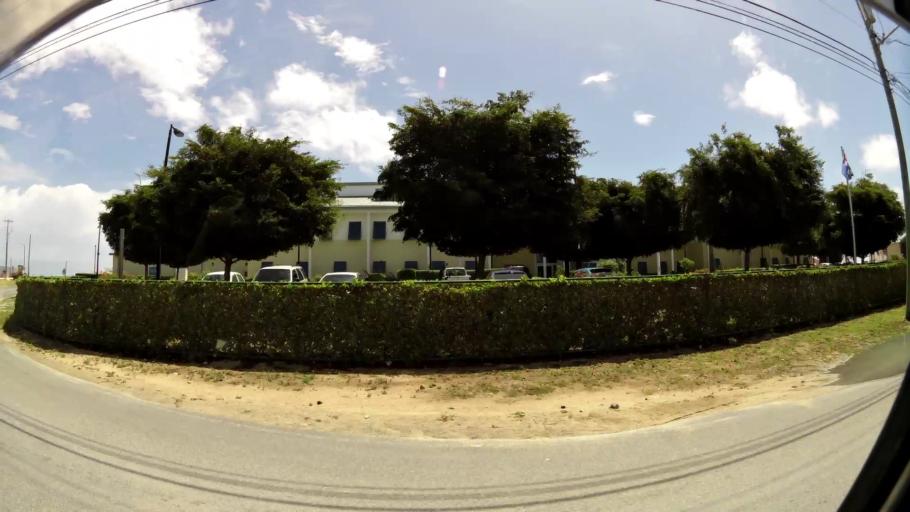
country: TC
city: Cockburn Town
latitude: 21.4804
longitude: -71.1444
